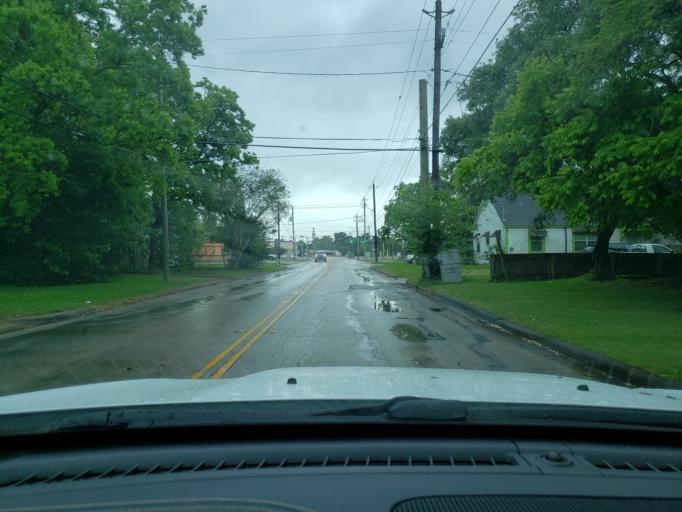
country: US
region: Texas
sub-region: Harris County
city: Baytown
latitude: 29.7480
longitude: -94.9728
